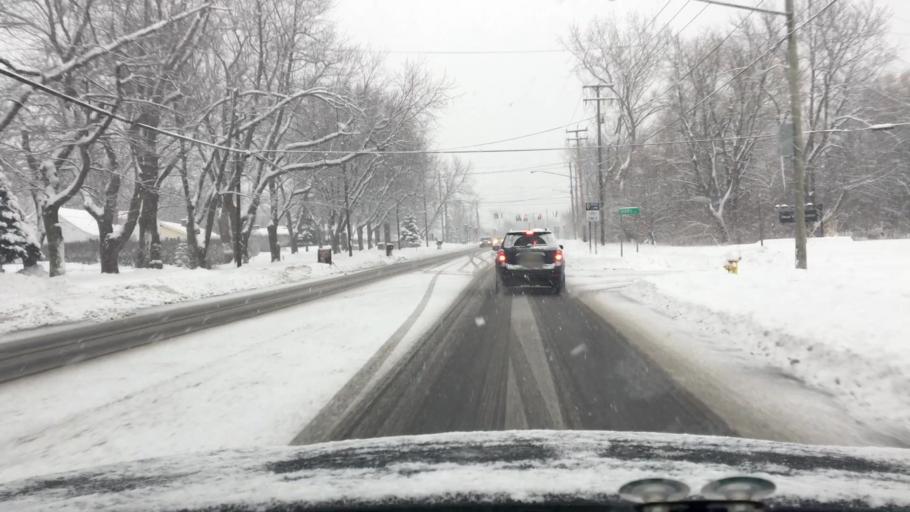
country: US
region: New York
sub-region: Erie County
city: Orchard Park
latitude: 42.7906
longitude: -78.7513
